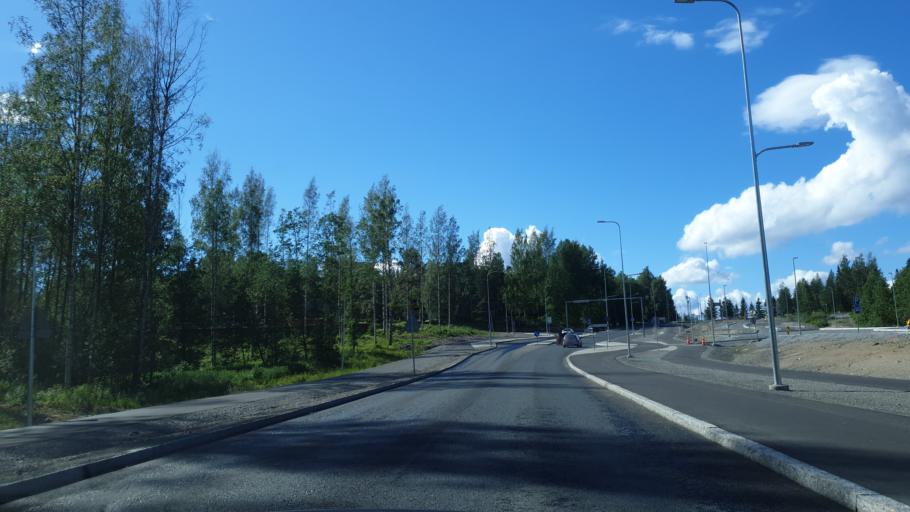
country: FI
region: Northern Savo
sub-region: Kuopio
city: Kuopio
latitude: 62.9042
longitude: 27.6563
